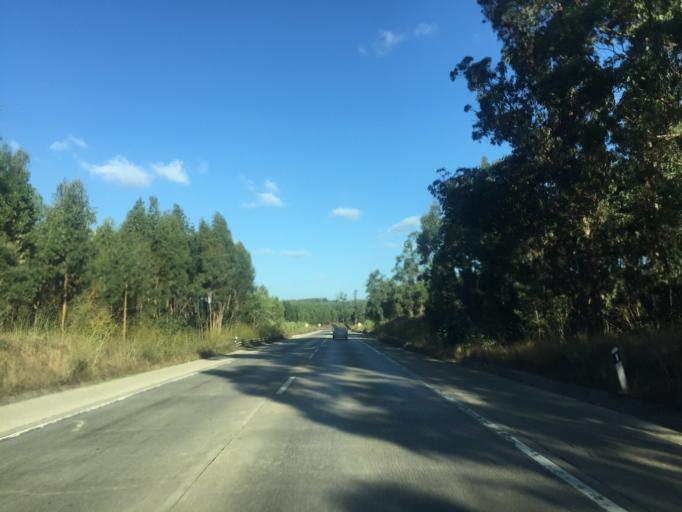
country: PT
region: Santarem
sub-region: Rio Maior
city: Rio Maior
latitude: 39.2905
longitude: -8.9456
